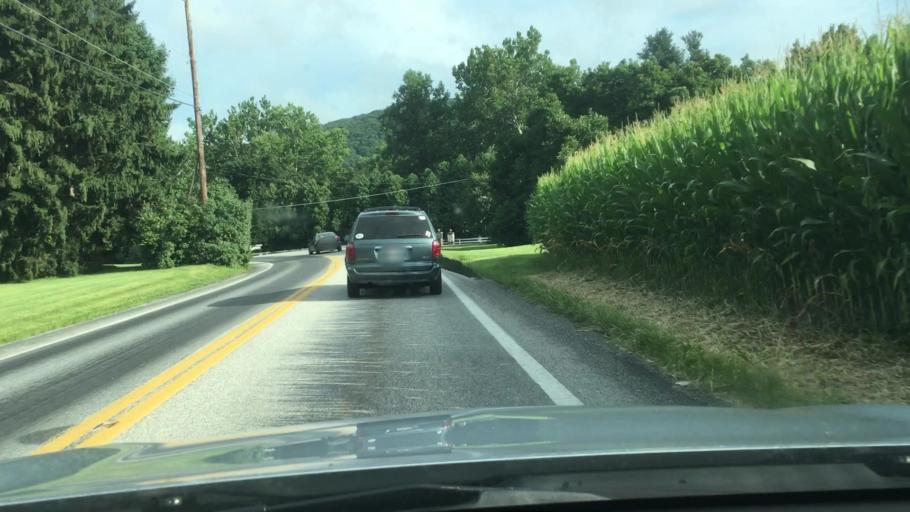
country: US
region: Pennsylvania
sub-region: York County
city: Dillsburg
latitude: 40.1465
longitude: -77.0644
